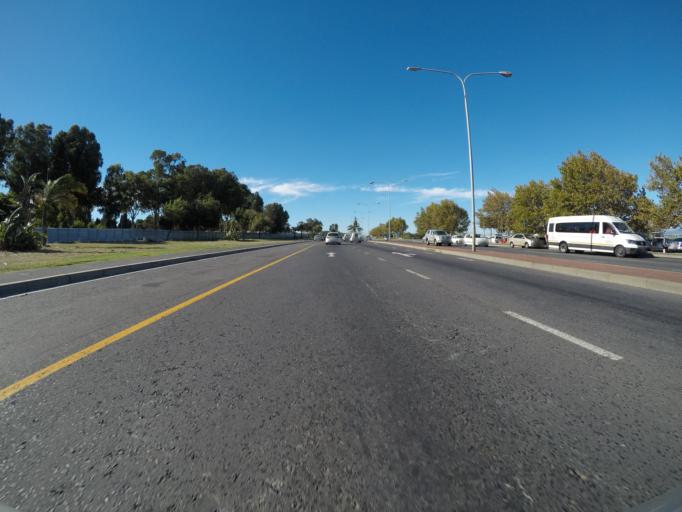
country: ZA
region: Western Cape
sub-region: City of Cape Town
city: Kraaifontein
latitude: -33.9104
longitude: 18.6657
